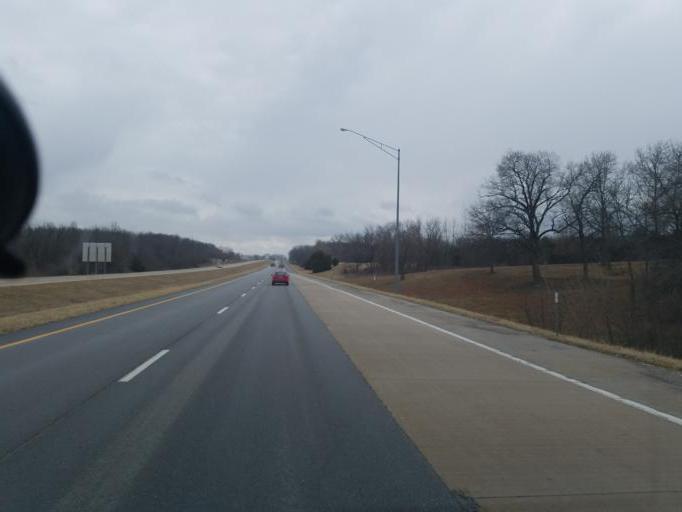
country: US
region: Missouri
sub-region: Randolph County
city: Moberly
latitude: 39.3896
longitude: -92.4134
